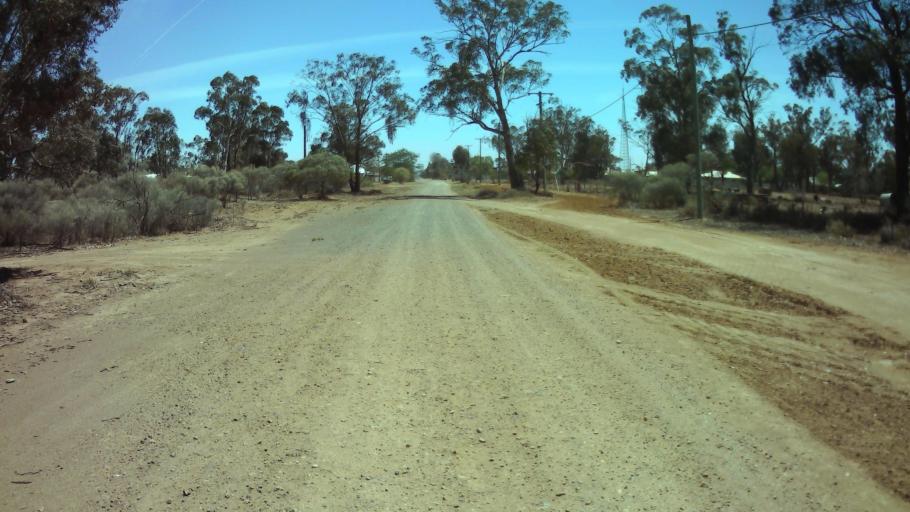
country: AU
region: New South Wales
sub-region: Weddin
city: Grenfell
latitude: -33.8464
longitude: 147.7385
